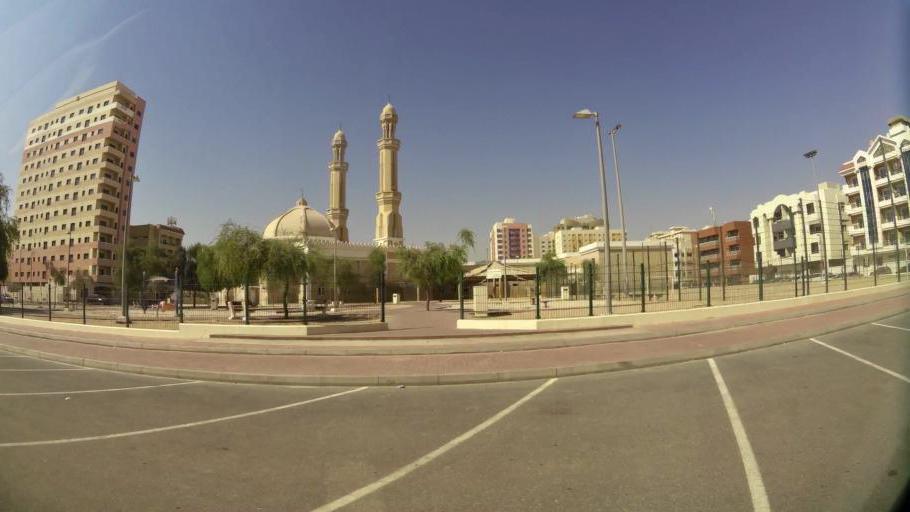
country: AE
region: Ash Shariqah
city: Sharjah
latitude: 25.2746
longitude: 55.3718
